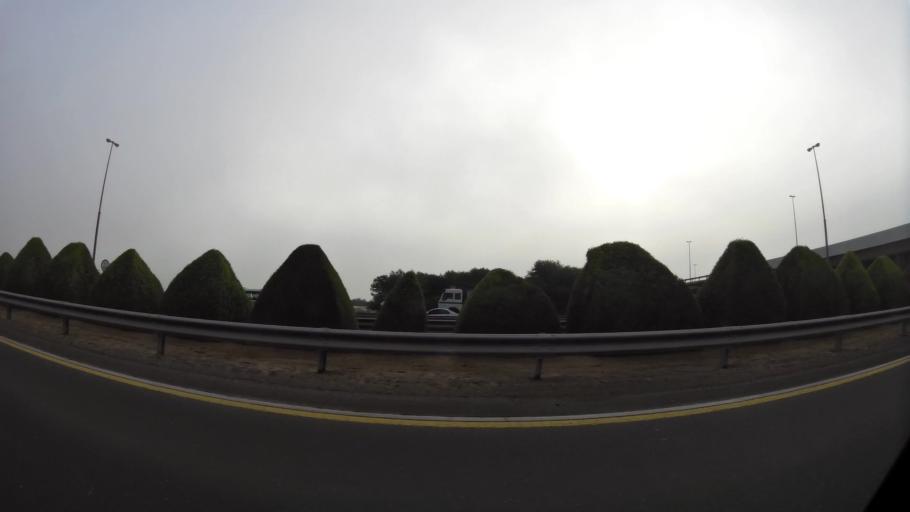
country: AE
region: Dubai
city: Dubai
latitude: 25.1749
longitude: 55.3206
